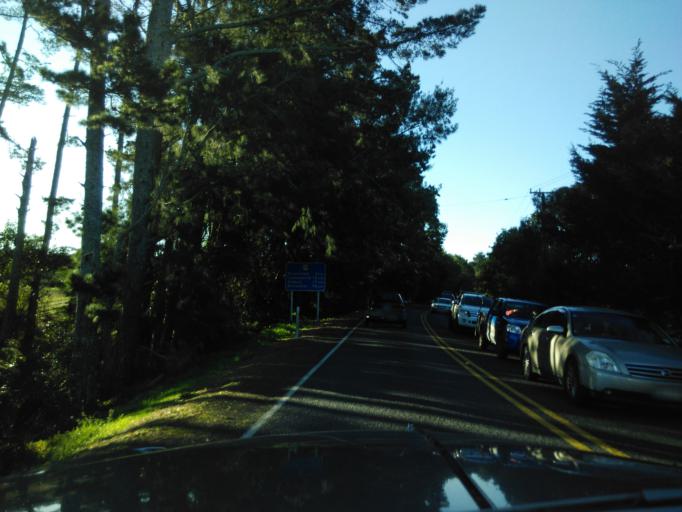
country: NZ
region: Auckland
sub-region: Auckland
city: Rosebank
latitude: -36.7848
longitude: 174.5841
